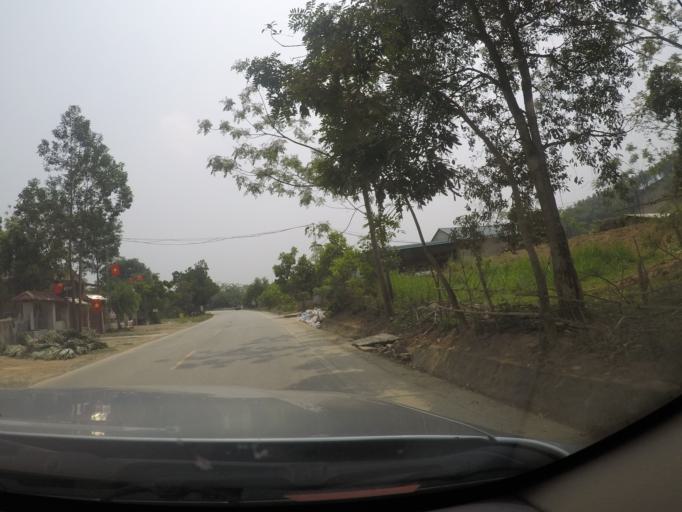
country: VN
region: Thanh Hoa
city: Thi Tran Yen Cat
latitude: 19.7424
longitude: 105.4239
